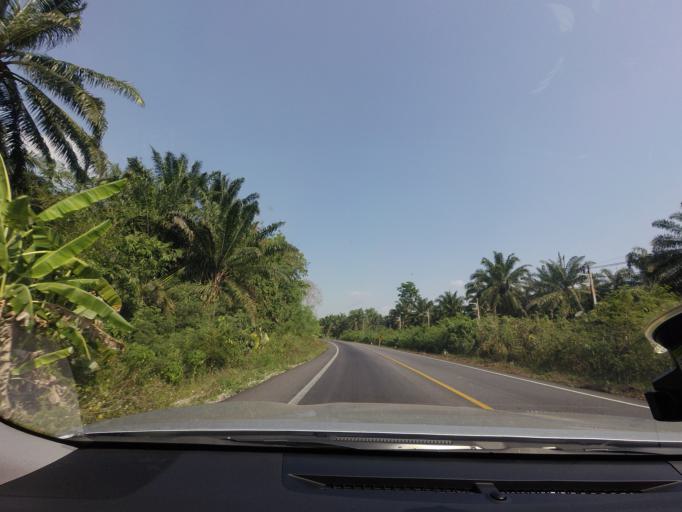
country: TH
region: Krabi
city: Plai Phraya
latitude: 8.5556
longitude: 98.7838
